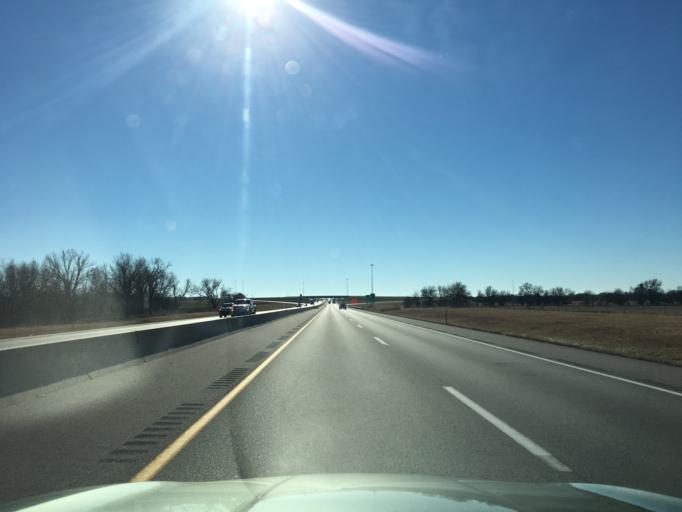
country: US
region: Kansas
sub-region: Sumner County
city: Wellington
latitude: 37.2862
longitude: -97.3403
